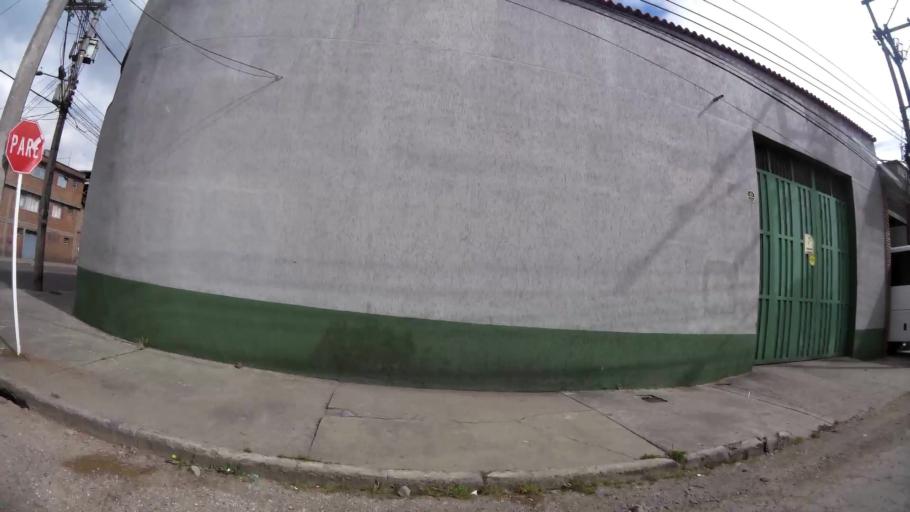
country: CO
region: Bogota D.C.
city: Bogota
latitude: 4.6182
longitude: -74.1045
